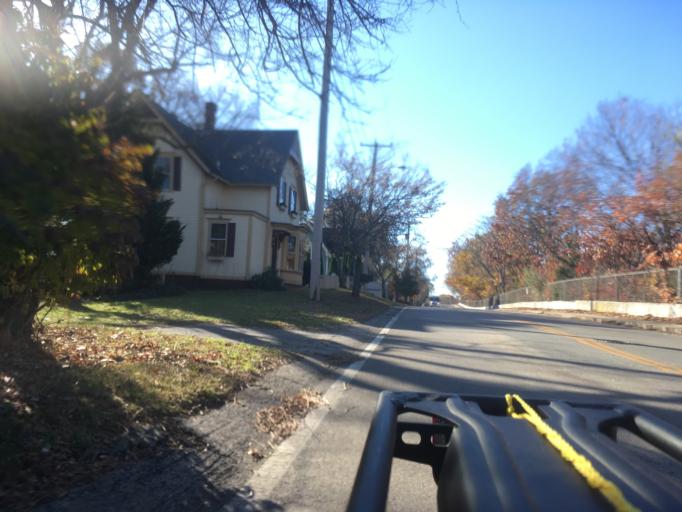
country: US
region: Rhode Island
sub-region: Kent County
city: East Greenwich
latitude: 41.6566
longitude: -71.4497
